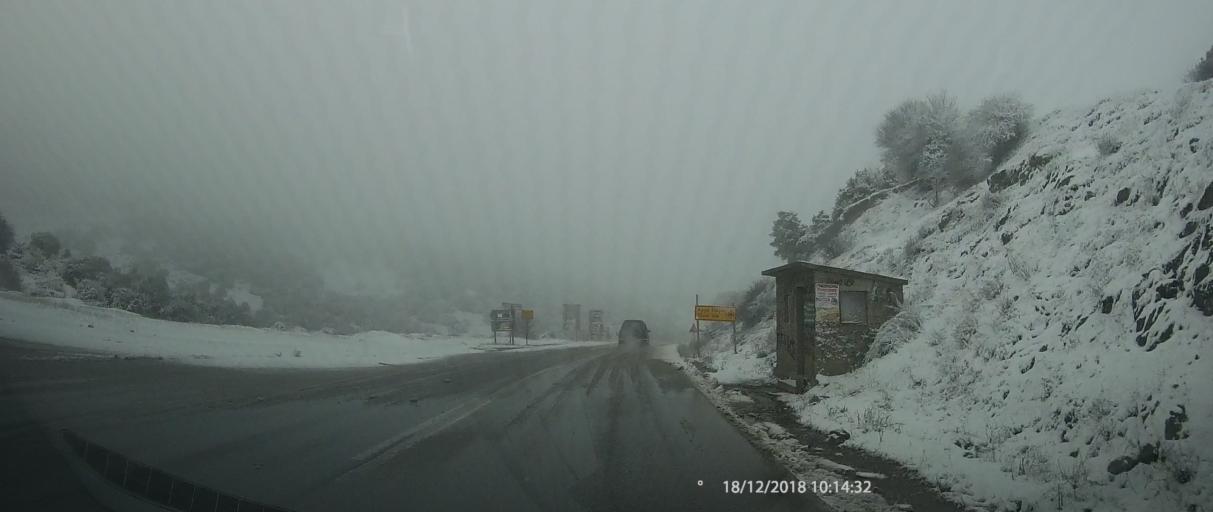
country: GR
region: Thessaly
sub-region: Nomos Larisis
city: Livadi
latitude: 40.1090
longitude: 22.2025
